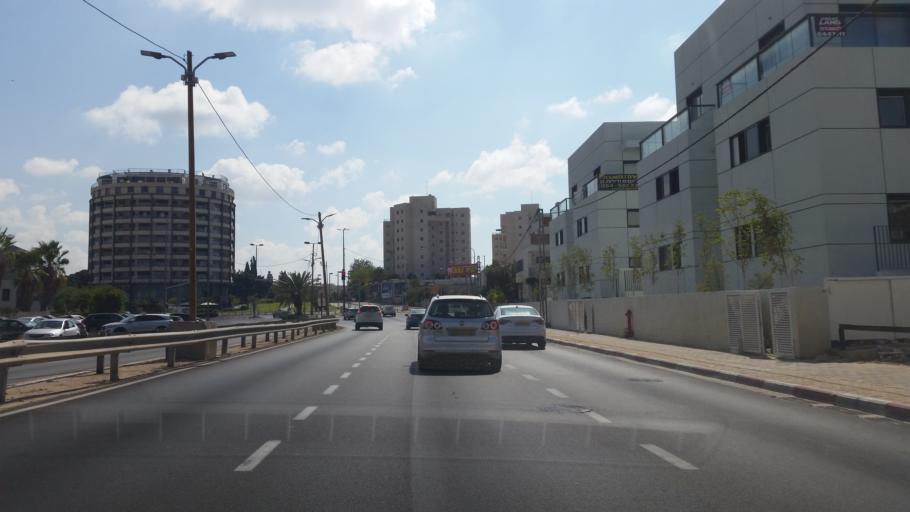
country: IL
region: Tel Aviv
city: Ramat HaSharon
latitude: 32.1248
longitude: 34.8249
